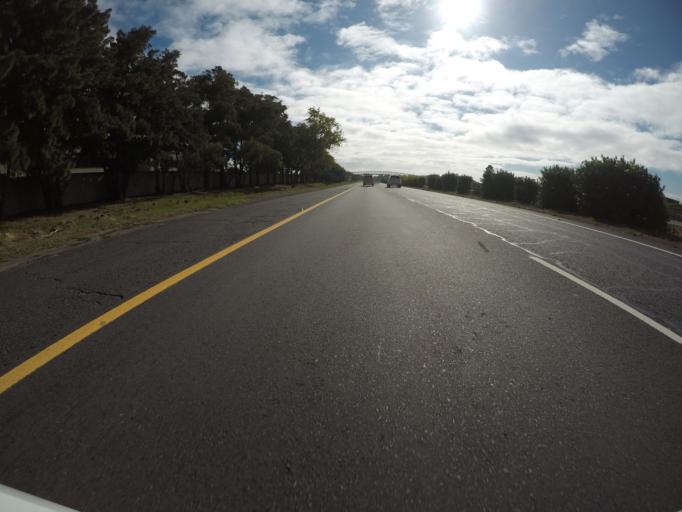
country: ZA
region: Western Cape
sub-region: City of Cape Town
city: Kraaifontein
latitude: -33.8502
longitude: 18.7073
